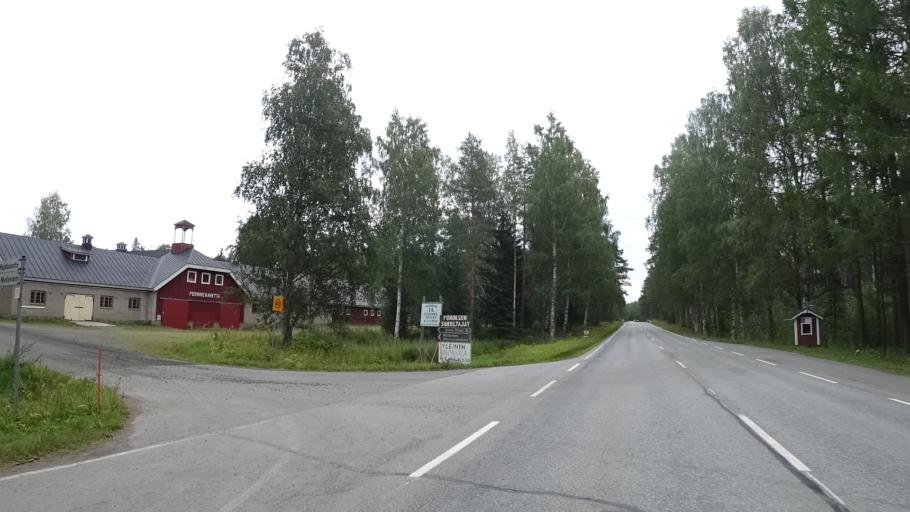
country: FI
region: North Karelia
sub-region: Keski-Karjala
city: Kesaelahti
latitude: 62.0934
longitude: 29.8699
